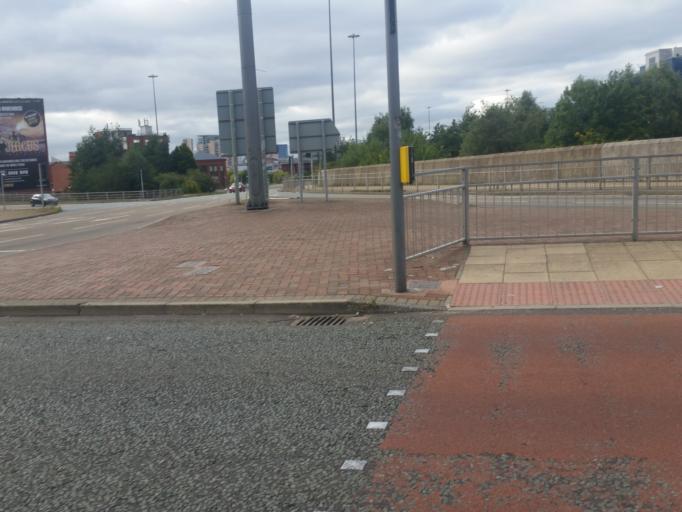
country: GB
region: England
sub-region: City and Borough of Salford
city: Salford
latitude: 53.4635
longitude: -2.2820
